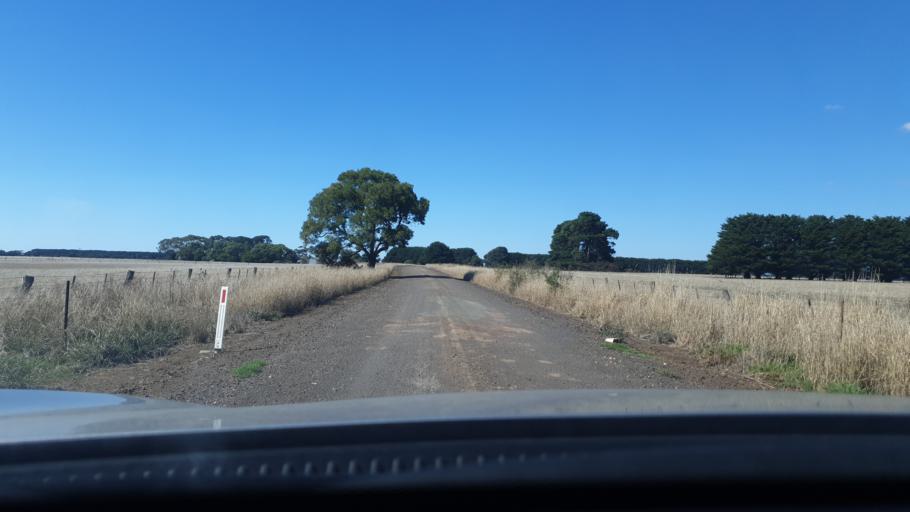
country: AU
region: Victoria
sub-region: Warrnambool
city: Warrnambool
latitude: -38.1657
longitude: 142.3696
